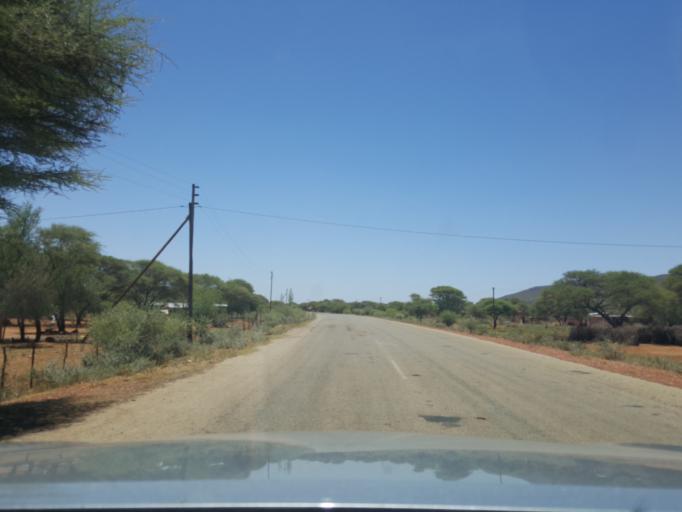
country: BW
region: South East
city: Ramotswa
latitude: -24.9717
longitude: 25.8969
